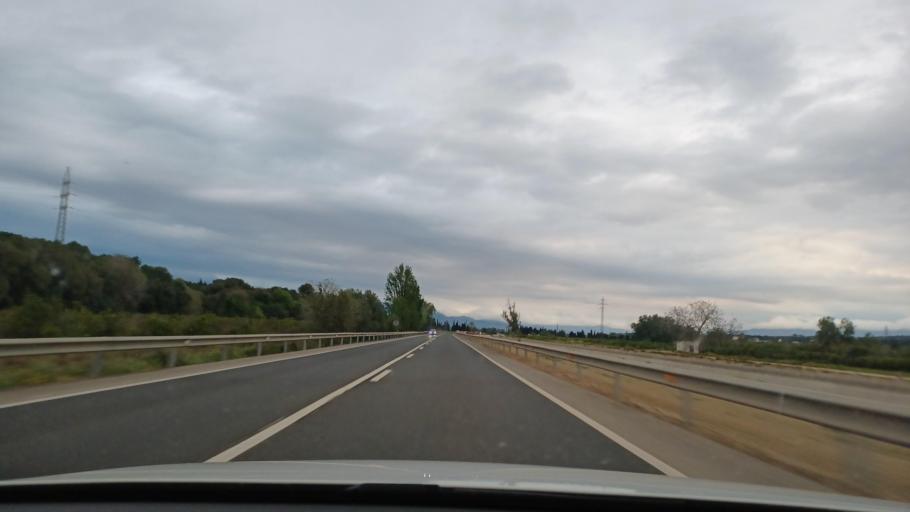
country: ES
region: Catalonia
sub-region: Provincia de Tarragona
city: Masdenverge
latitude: 40.7602
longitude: 0.5350
